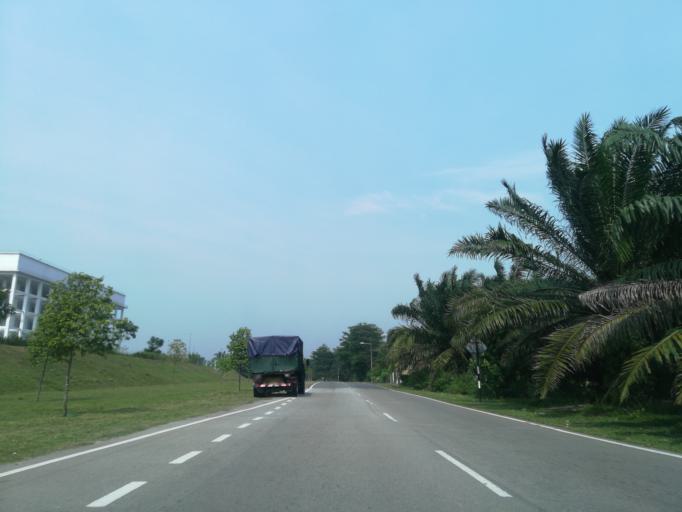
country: MY
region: Penang
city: Tasek Glugor
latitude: 5.4526
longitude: 100.5554
